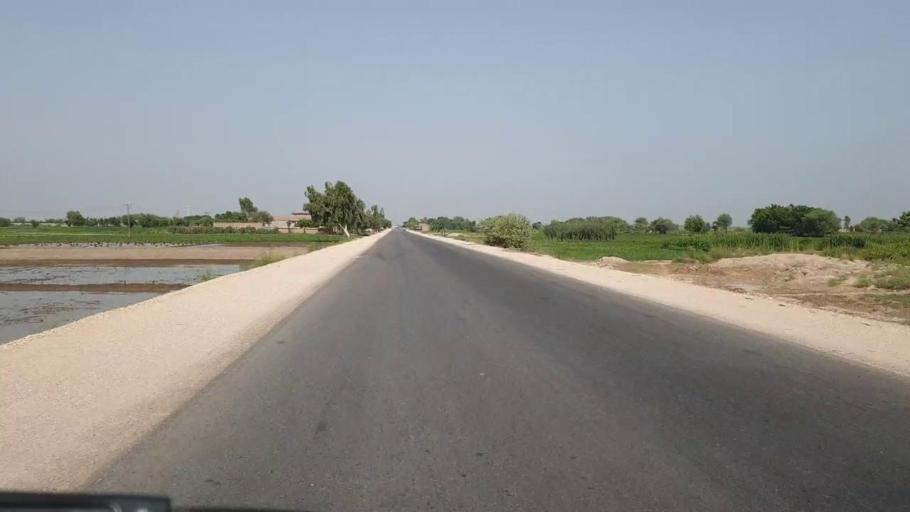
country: PK
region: Sindh
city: Sakrand
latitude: 26.2450
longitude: 68.2489
